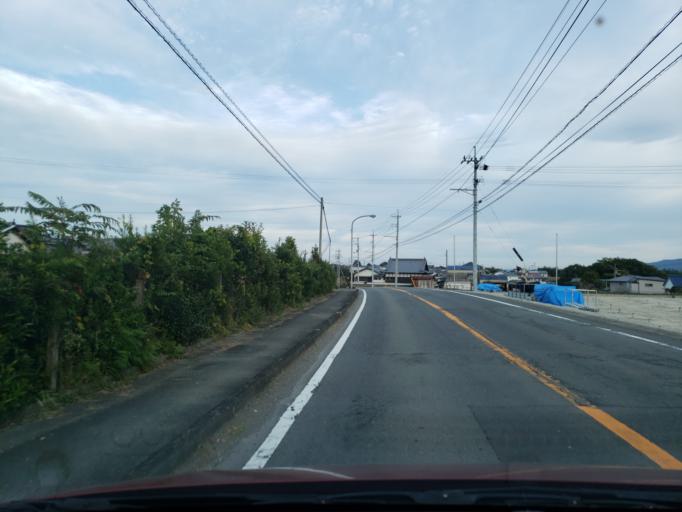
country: JP
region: Tokushima
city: Kamojimacho-jogejima
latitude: 34.0790
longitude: 134.2520
